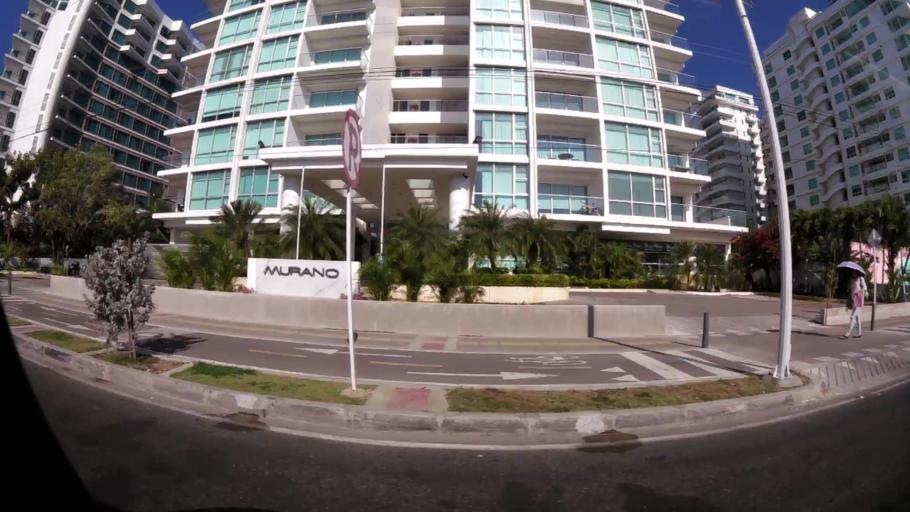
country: CO
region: Bolivar
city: Cartagena
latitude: 10.4644
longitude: -75.5018
